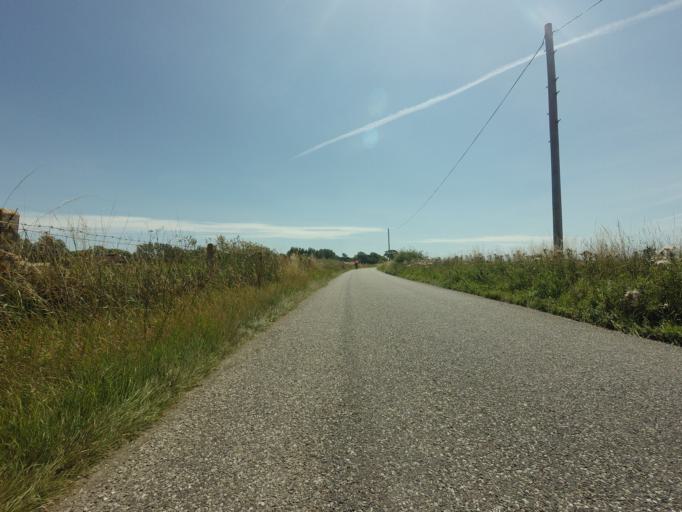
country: GB
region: England
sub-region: Kent
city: Lydd
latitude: 50.9621
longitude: 0.9029
